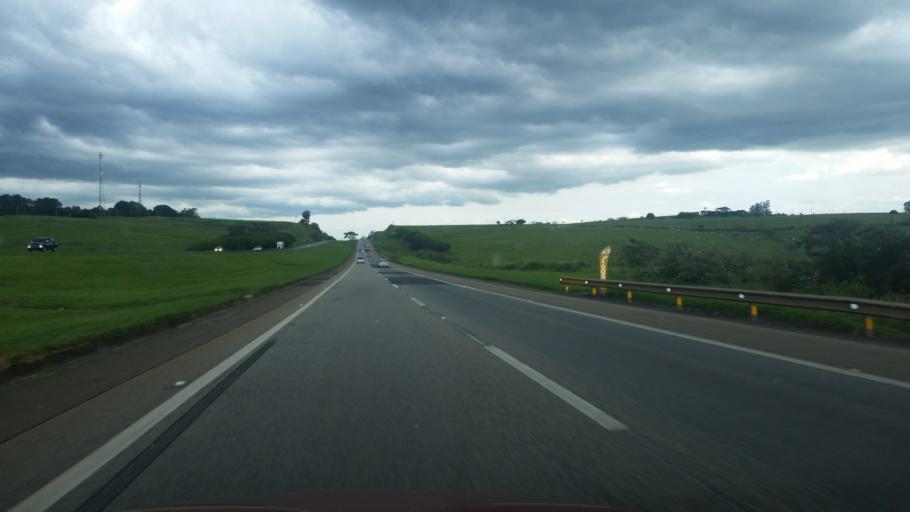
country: BR
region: Sao Paulo
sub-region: Boituva
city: Boituva
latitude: -23.3190
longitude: -47.6095
